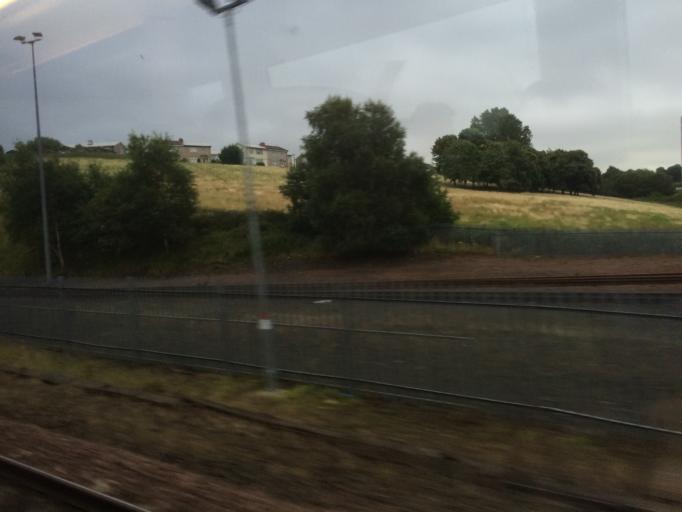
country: GB
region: Scotland
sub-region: East Dunbartonshire
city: Bishopbriggs
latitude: 55.8924
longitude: -4.2403
